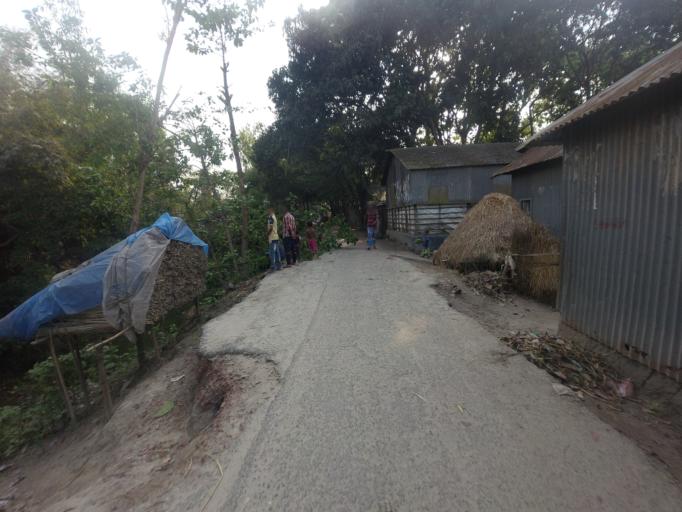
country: BD
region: Rajshahi
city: Sirajganj
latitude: 24.3246
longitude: 89.7130
